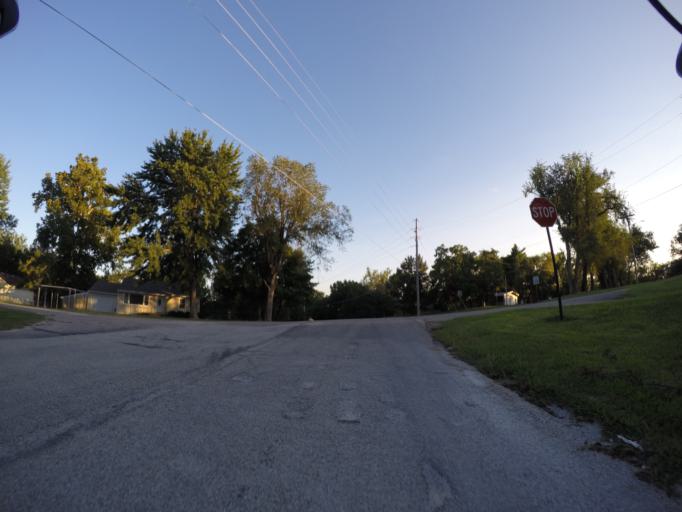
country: US
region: Kansas
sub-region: Riley County
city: Ogden
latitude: 39.1179
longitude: -96.7113
